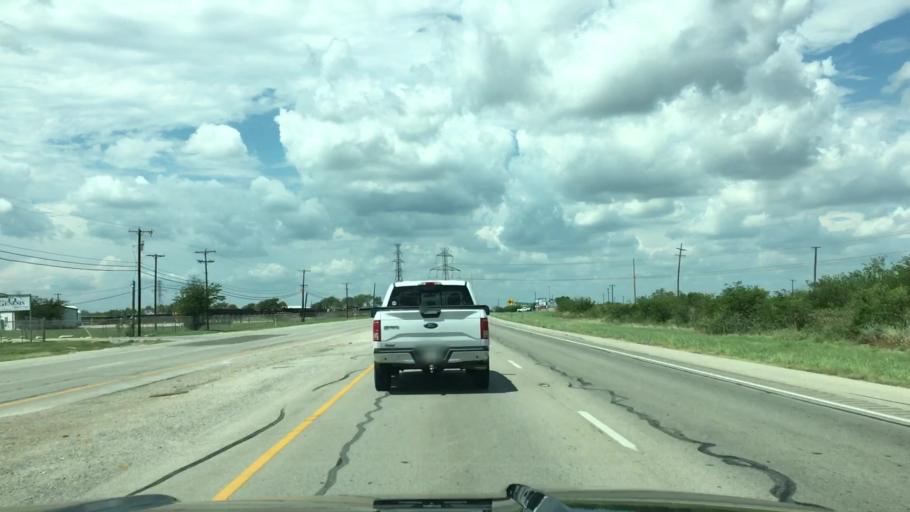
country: US
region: Texas
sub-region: Tarrant County
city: Eagle Mountain
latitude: 32.9023
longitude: -97.4004
